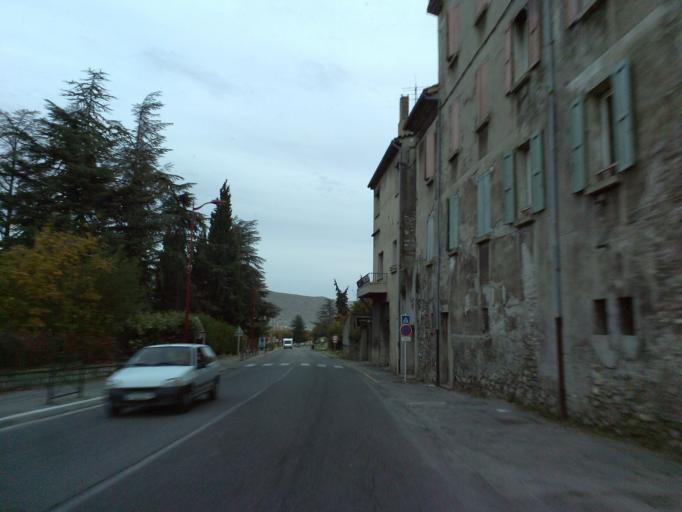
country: FR
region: Provence-Alpes-Cote d'Azur
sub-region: Departement des Alpes-de-Haute-Provence
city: Volonne
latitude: 44.0921
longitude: 6.0092
